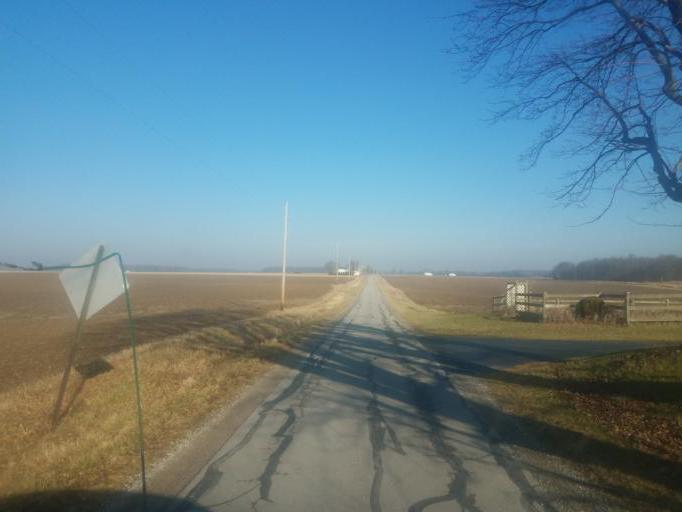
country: US
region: Ohio
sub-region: Huron County
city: Willard
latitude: 41.0249
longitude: -82.9392
